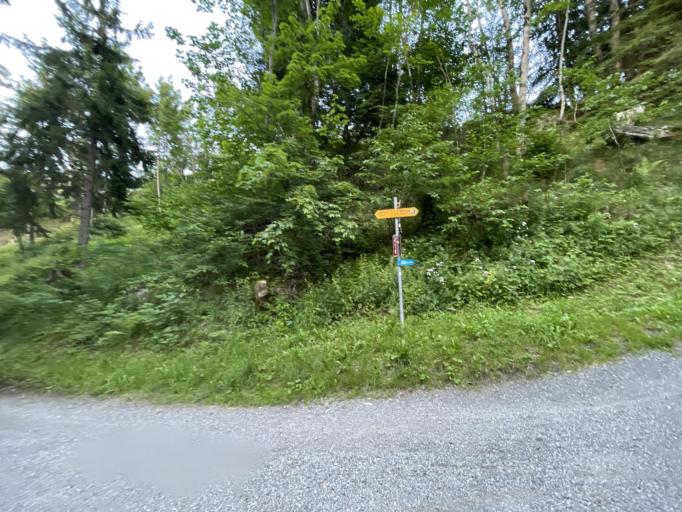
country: CH
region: Bern
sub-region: Interlaken-Oberhasli District
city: Lauterbrunnen
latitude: 46.6015
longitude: 7.9200
